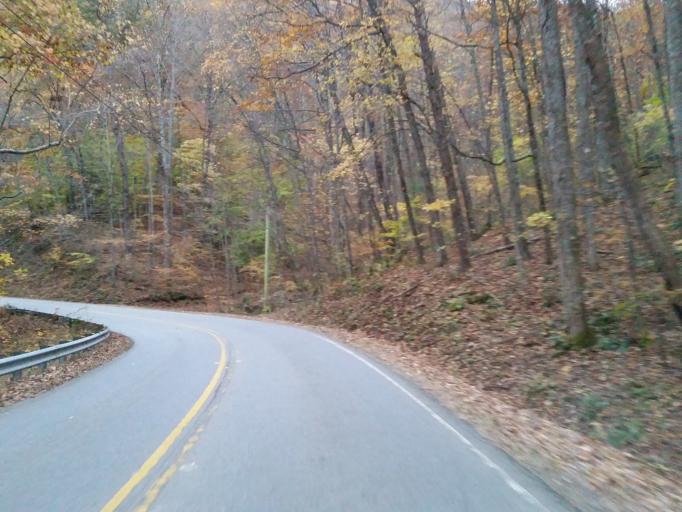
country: US
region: Georgia
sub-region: Lumpkin County
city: Dahlonega
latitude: 34.7026
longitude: -84.0463
